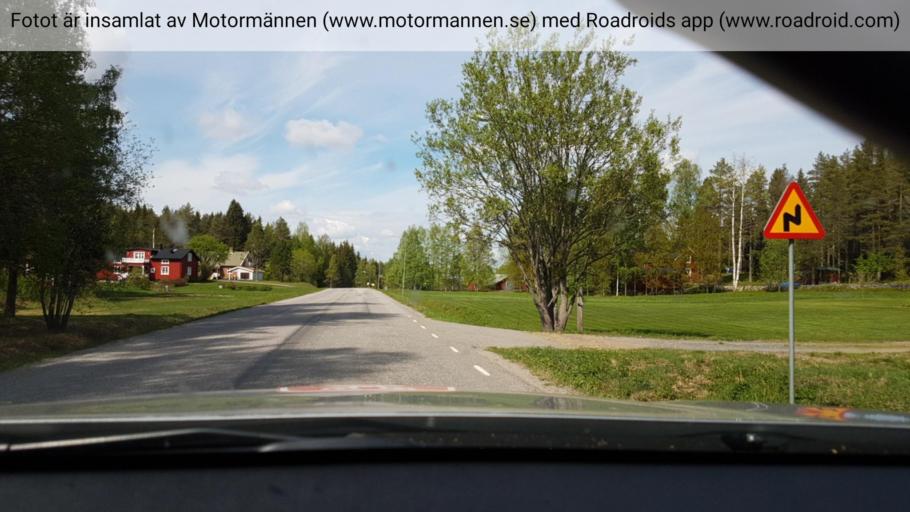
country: SE
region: Vaesterbotten
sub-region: Umea Kommun
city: Roback
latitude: 63.8674
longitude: 20.0485
